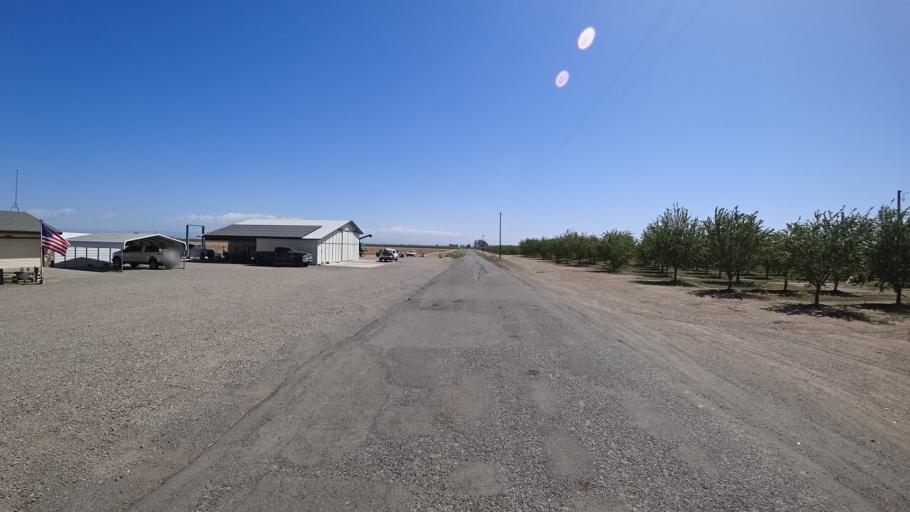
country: US
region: California
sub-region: Glenn County
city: Orland
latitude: 39.6817
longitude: -122.1497
